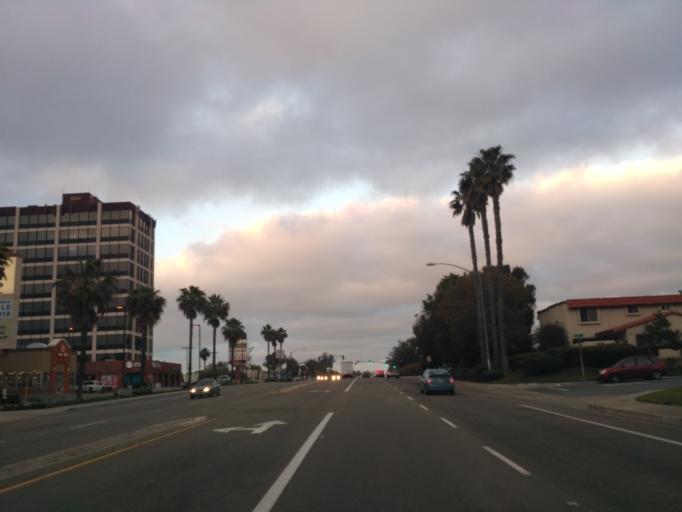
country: US
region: California
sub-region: San Diego County
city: La Jolla
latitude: 32.8185
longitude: -117.1842
